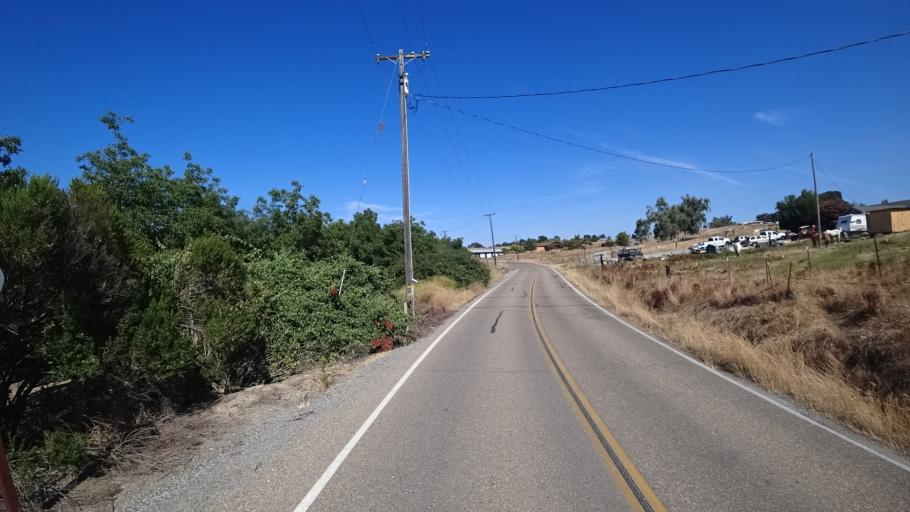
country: US
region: California
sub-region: Calaveras County
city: Rancho Calaveras
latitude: 38.0989
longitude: -120.8850
